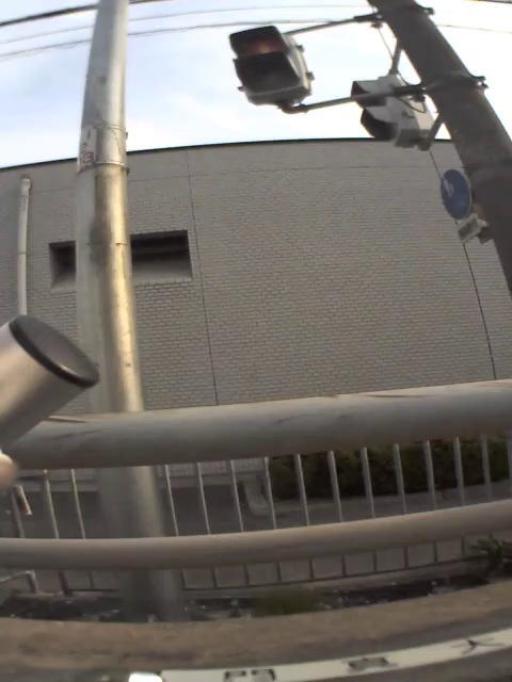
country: JP
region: Osaka
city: Kadoma
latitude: 34.7342
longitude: 135.5955
